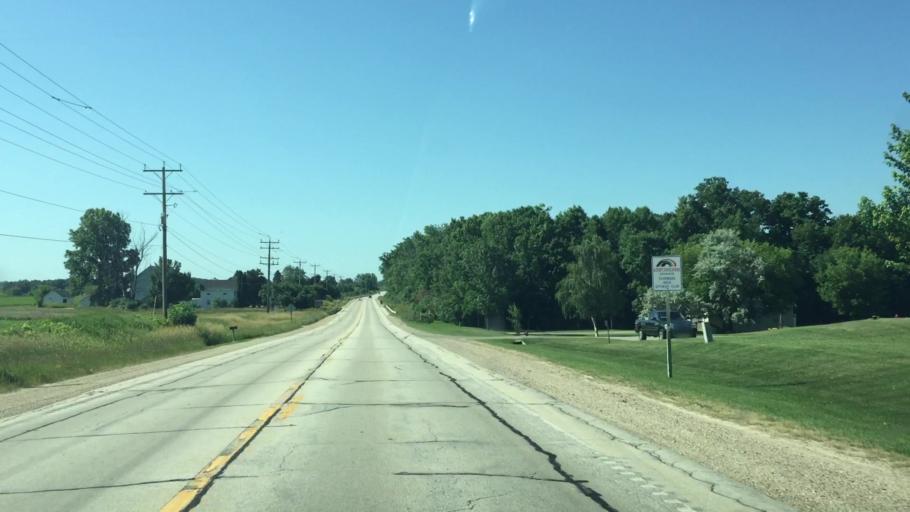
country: US
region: Wisconsin
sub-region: Calumet County
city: Sherwood
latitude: 44.1604
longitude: -88.2650
